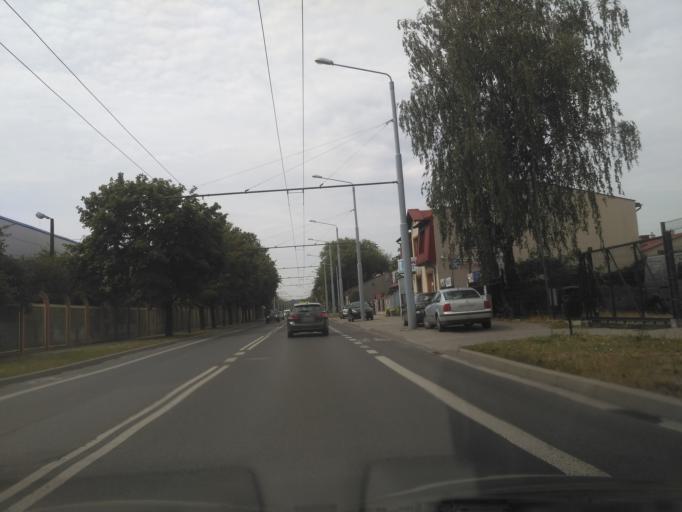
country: PL
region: Lublin Voivodeship
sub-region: Powiat lubelski
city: Lublin
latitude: 51.2251
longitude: 22.5499
